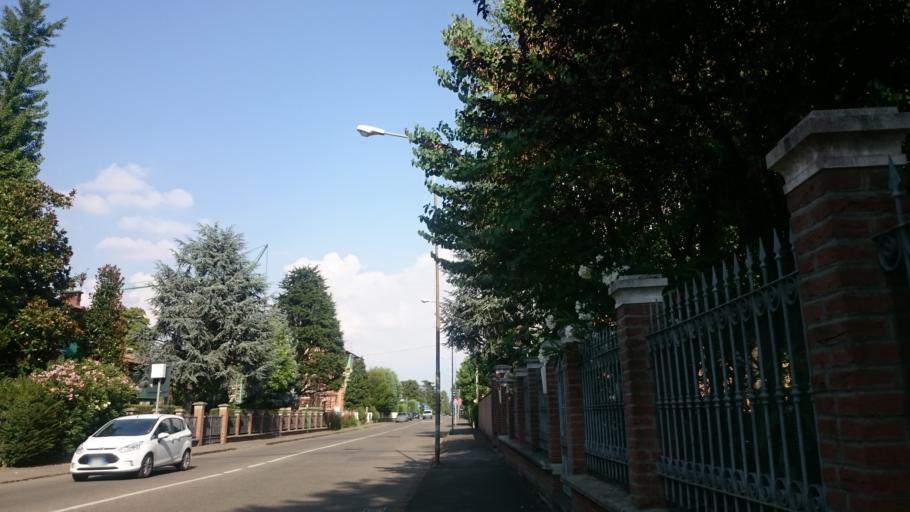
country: IT
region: Emilia-Romagna
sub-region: Provincia di Reggio Emilia
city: Rubiera
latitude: 44.6499
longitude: 10.7782
